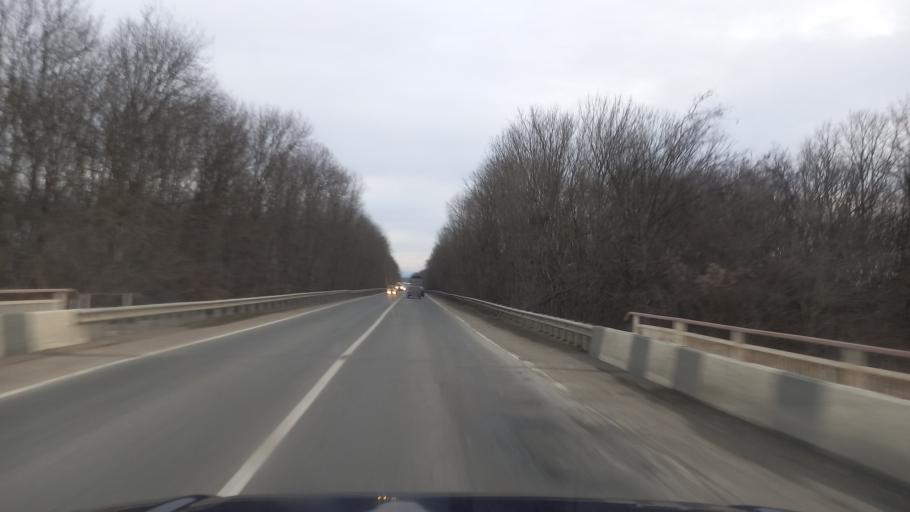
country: RU
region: Krasnodarskiy
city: Belorechensk
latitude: 44.7610
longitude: 39.9157
